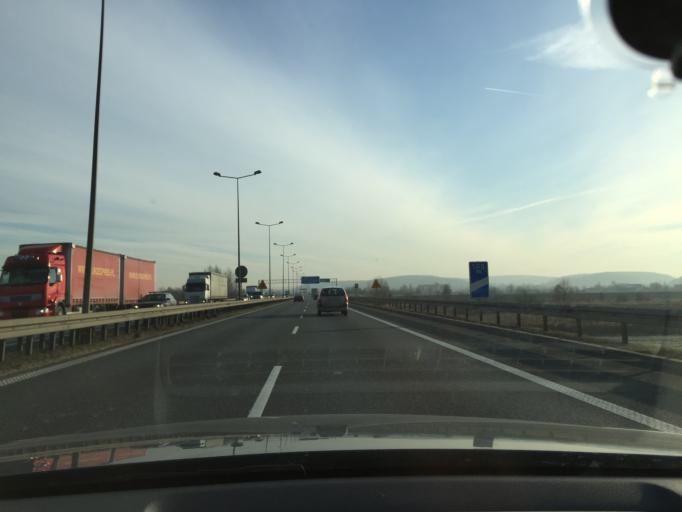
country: PL
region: Lesser Poland Voivodeship
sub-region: Powiat krakowski
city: Kryspinow
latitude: 50.0391
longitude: 19.8107
